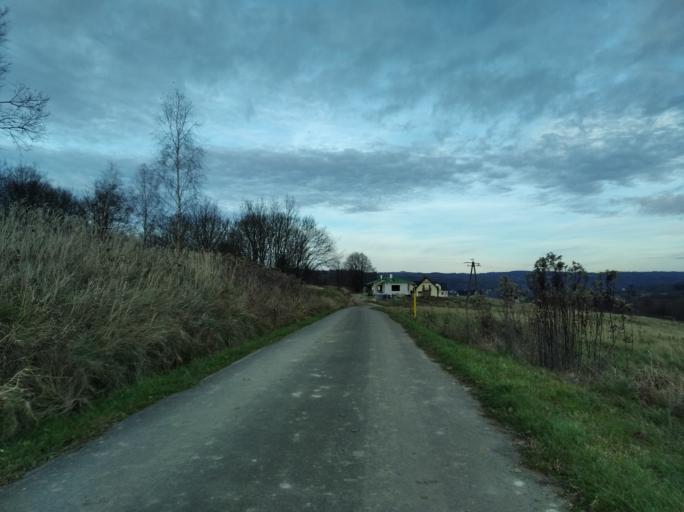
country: PL
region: Subcarpathian Voivodeship
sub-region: Powiat brzozowski
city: Domaradz
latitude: 49.7834
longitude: 21.9371
